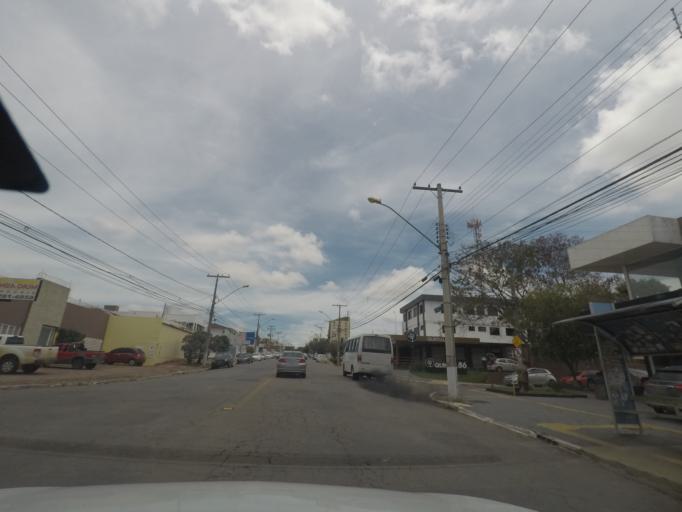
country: BR
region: Goias
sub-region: Goiania
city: Goiania
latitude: -16.6868
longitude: -49.2484
